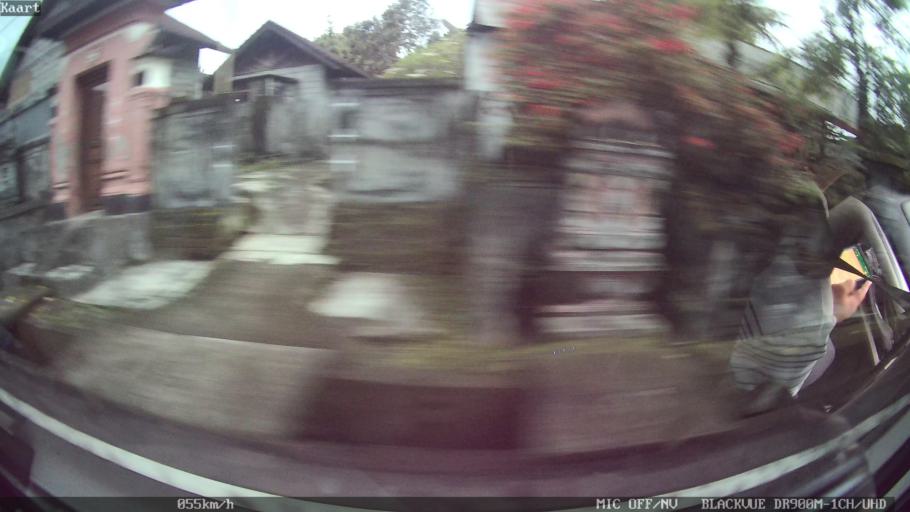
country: ID
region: Bali
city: Banjar Sayanbaleran
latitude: -8.5148
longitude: 115.1875
